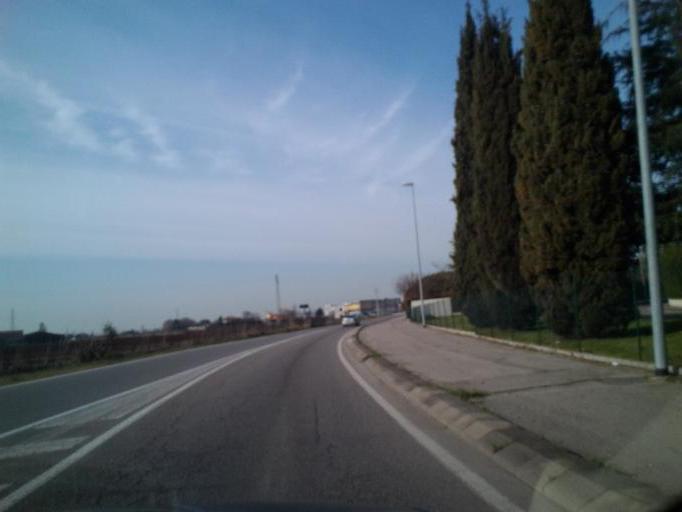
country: IT
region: Veneto
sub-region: Provincia di Verona
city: Villafranca di Verona
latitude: 45.3455
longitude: 10.8429
